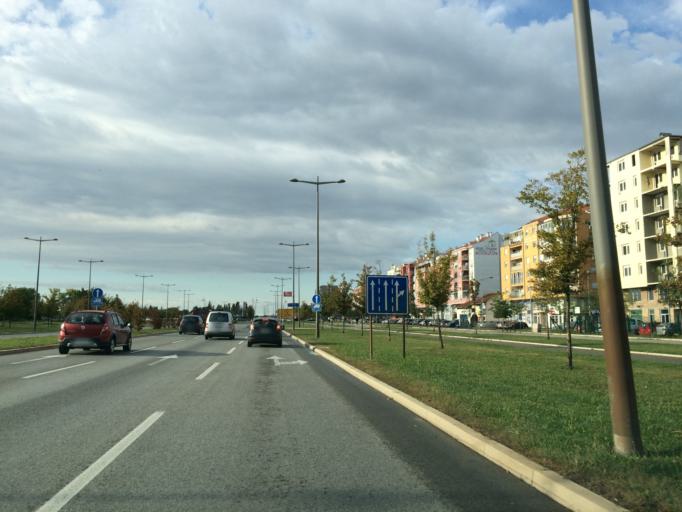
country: RS
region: Autonomna Pokrajina Vojvodina
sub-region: Juznobacki Okrug
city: Novi Sad
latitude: 45.2578
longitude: 19.8105
